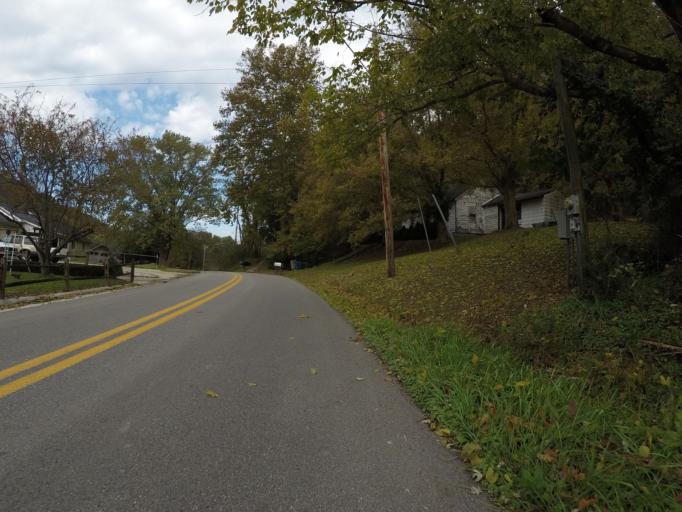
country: US
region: West Virginia
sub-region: Wayne County
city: Lavalette
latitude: 38.3397
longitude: -82.4497
